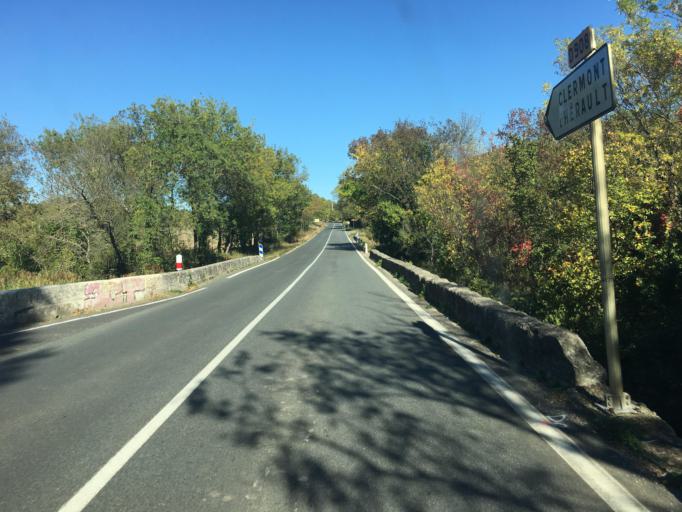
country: FR
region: Languedoc-Roussillon
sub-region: Departement de l'Herault
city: Nebian
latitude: 43.6116
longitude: 3.4046
